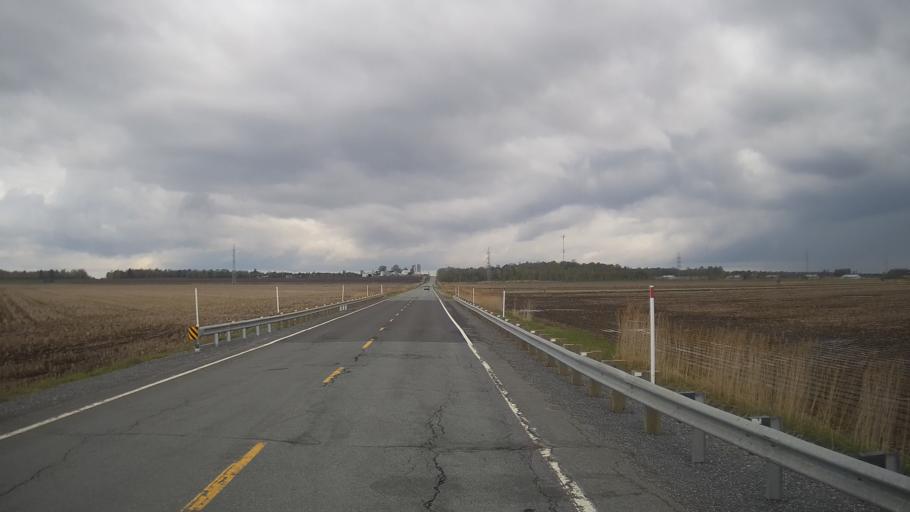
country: CA
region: Quebec
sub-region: Monteregie
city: Farnham
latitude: 45.2604
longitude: -72.9250
